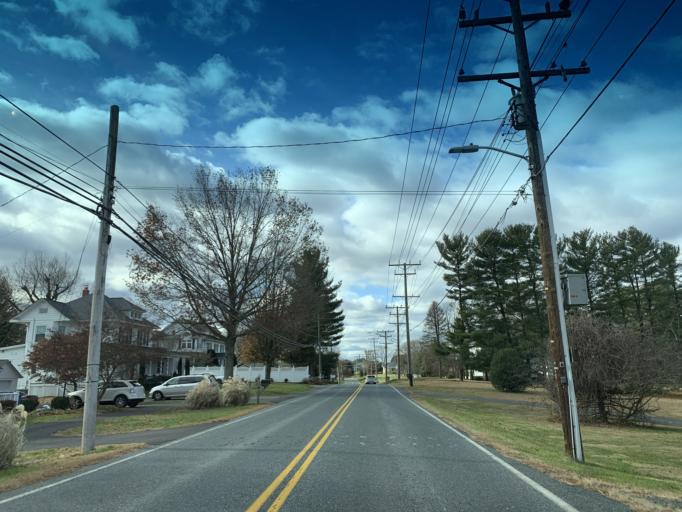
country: US
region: Maryland
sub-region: Harford County
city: Bel Air North
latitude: 39.5847
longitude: -76.3910
